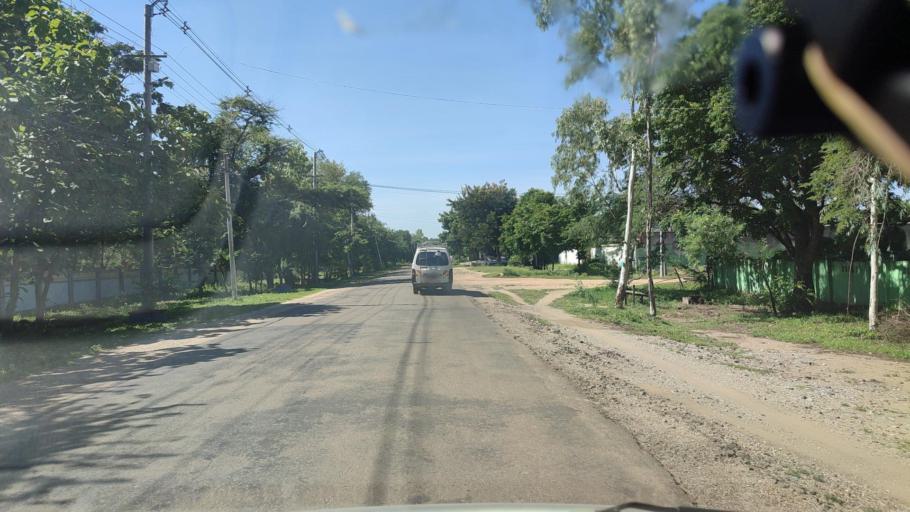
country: MM
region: Magway
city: Taungdwingyi
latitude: 19.9888
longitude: 95.5517
